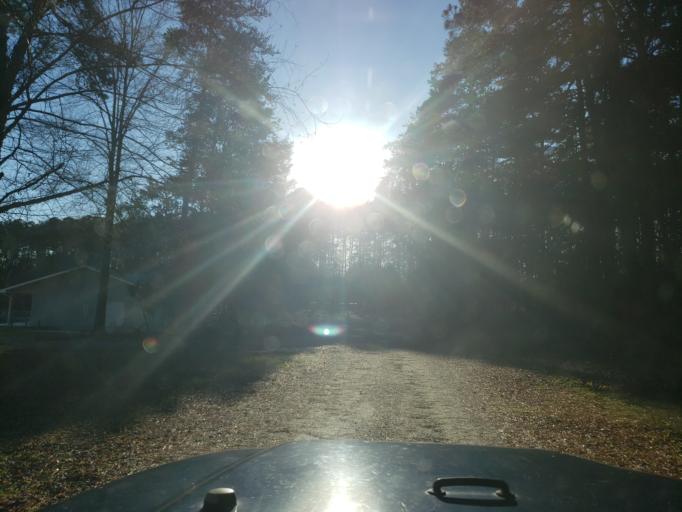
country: US
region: North Carolina
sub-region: Lincoln County
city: Westport
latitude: 35.5201
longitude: -80.9180
